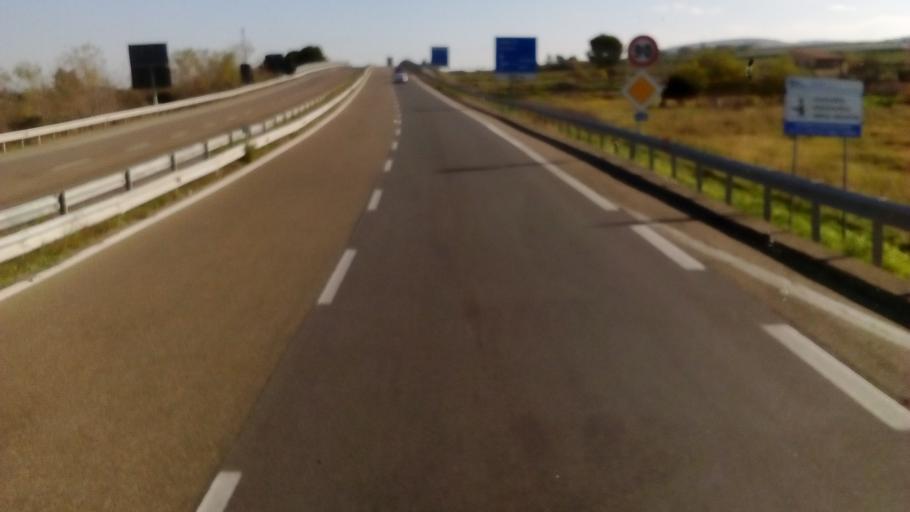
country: IT
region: Basilicate
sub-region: Provincia di Potenza
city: Zona 179
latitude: 41.0871
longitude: 15.5987
